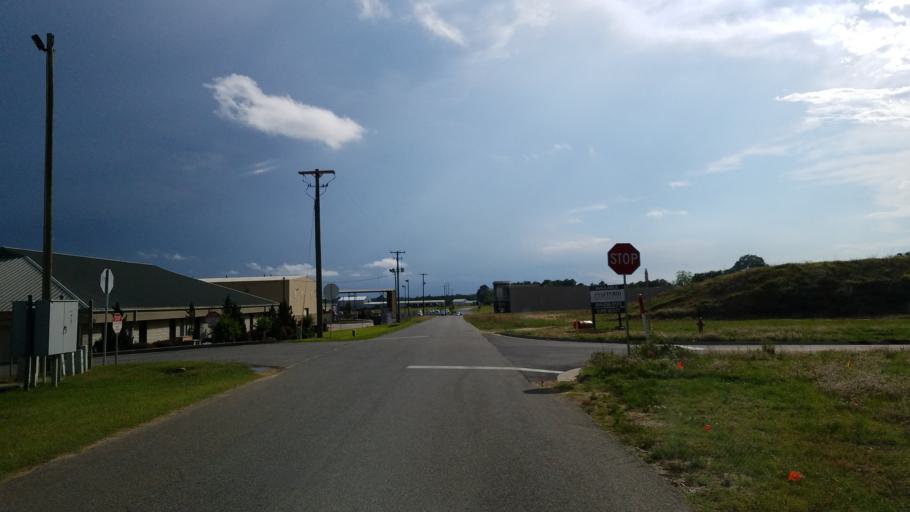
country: US
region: Georgia
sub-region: Tift County
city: Tifton
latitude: 31.4479
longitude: -83.5413
